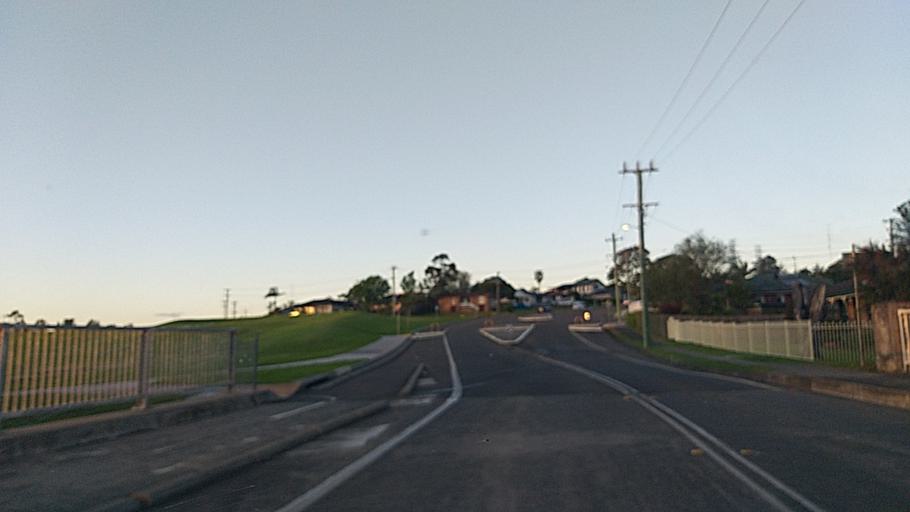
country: AU
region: New South Wales
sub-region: Wollongong
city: Koonawarra
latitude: -34.5021
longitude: 150.8138
